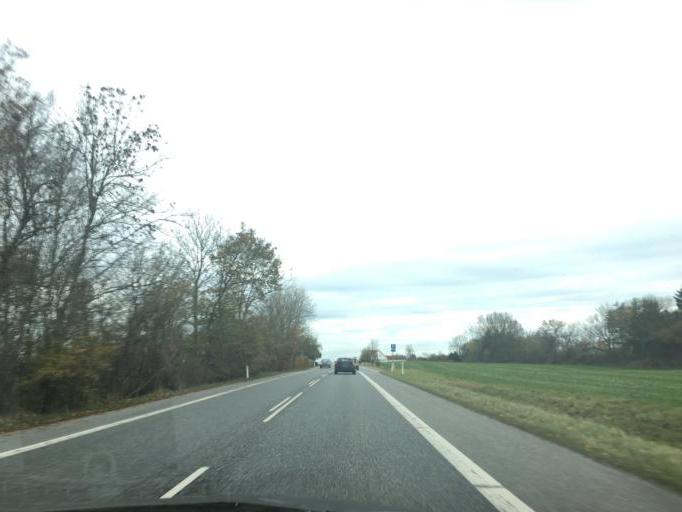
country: DK
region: South Denmark
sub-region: Vejle Kommune
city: Vejle
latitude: 55.6479
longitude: 9.5013
